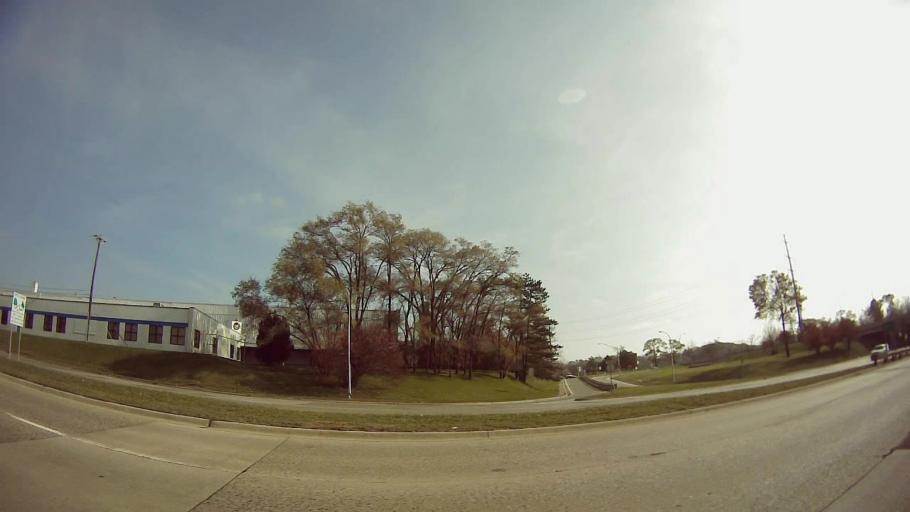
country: US
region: Michigan
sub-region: Wayne County
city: Redford
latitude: 42.4440
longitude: -83.2783
